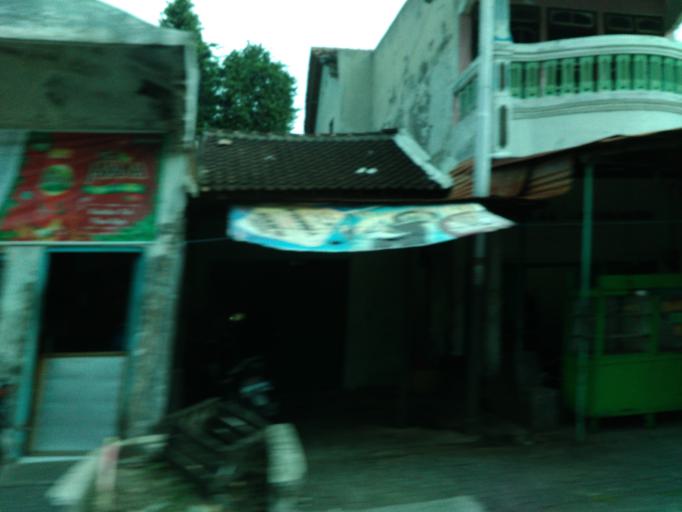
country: ID
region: Central Java
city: Delanggu
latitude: -7.6221
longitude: 110.7064
